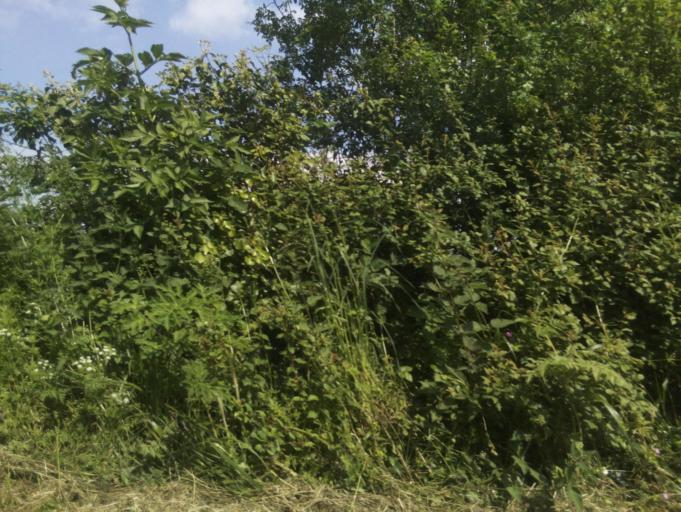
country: GB
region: England
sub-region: Wiltshire
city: Luckington
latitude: 51.5831
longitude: -2.2682
